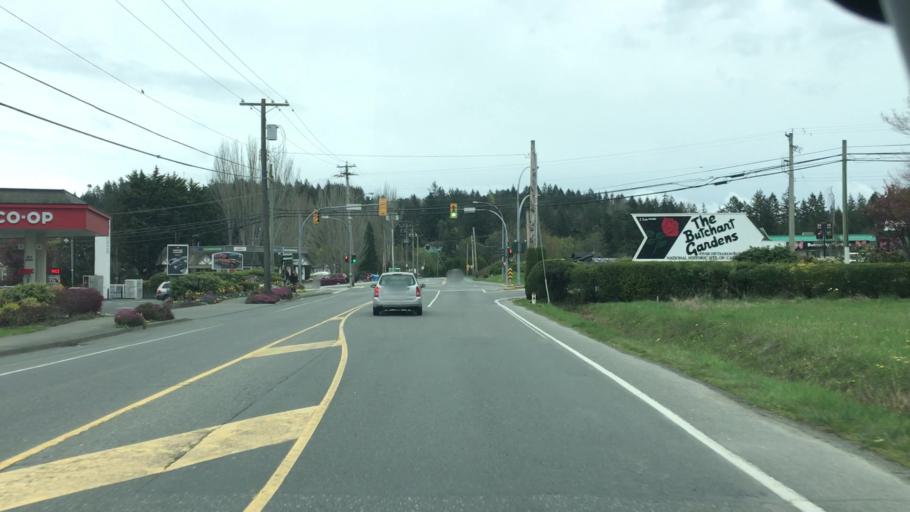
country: CA
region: British Columbia
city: North Saanich
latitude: 48.5658
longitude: -123.4390
